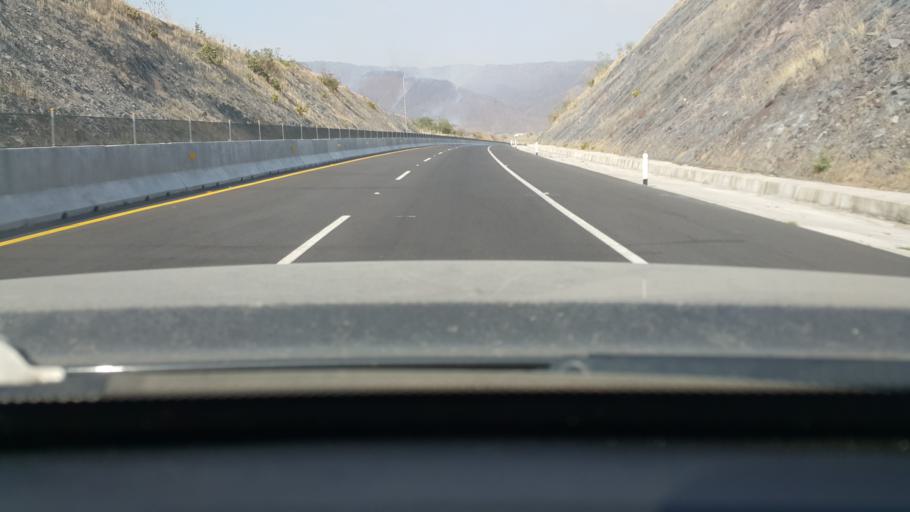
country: MX
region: Nayarit
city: Jala
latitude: 21.0736
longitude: -104.4538
